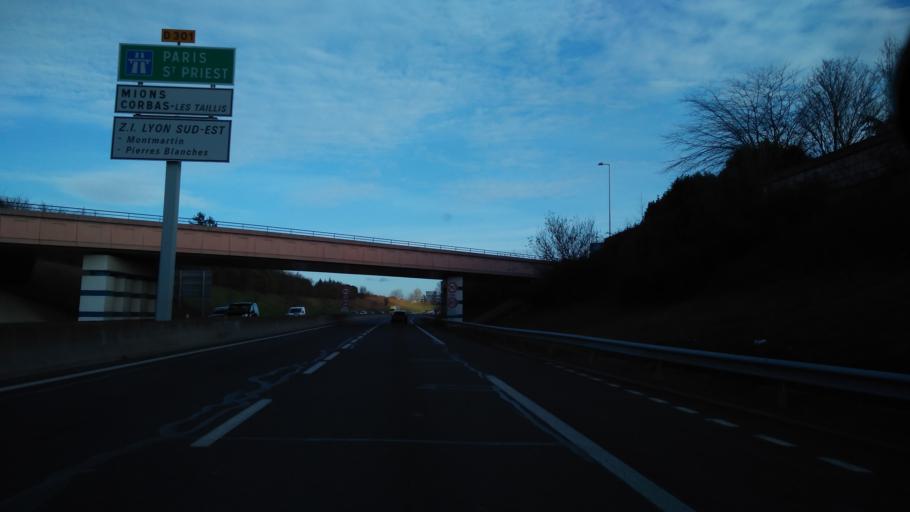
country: FR
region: Rhone-Alpes
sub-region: Departement du Rhone
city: Corbas
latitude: 45.6801
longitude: 4.8938
